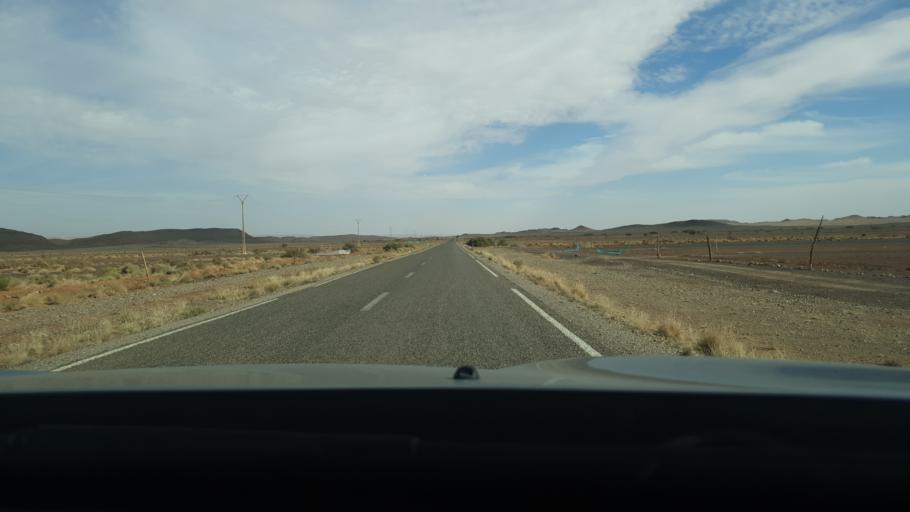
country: MA
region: Meknes-Tafilalet
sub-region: Errachidia
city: Goulmima
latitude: 31.5696
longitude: -4.8094
